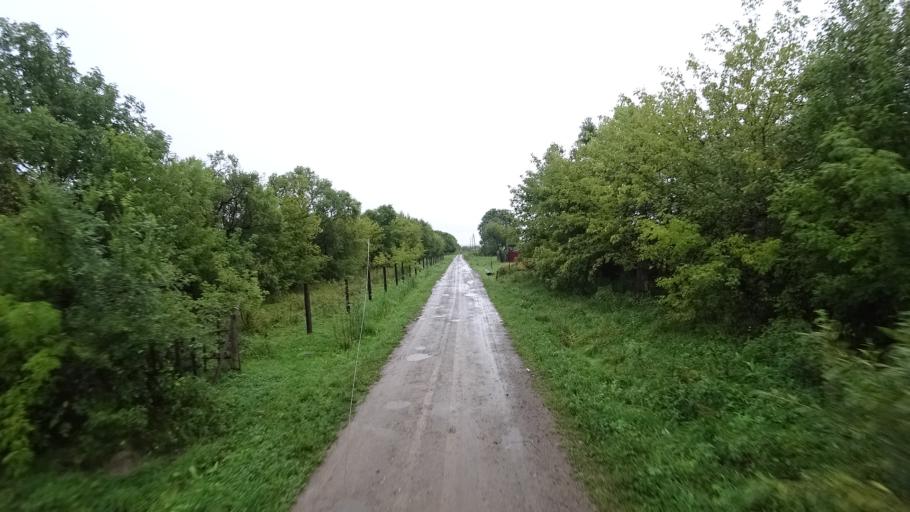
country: RU
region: Primorskiy
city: Monastyrishche
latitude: 44.2515
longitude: 132.4260
